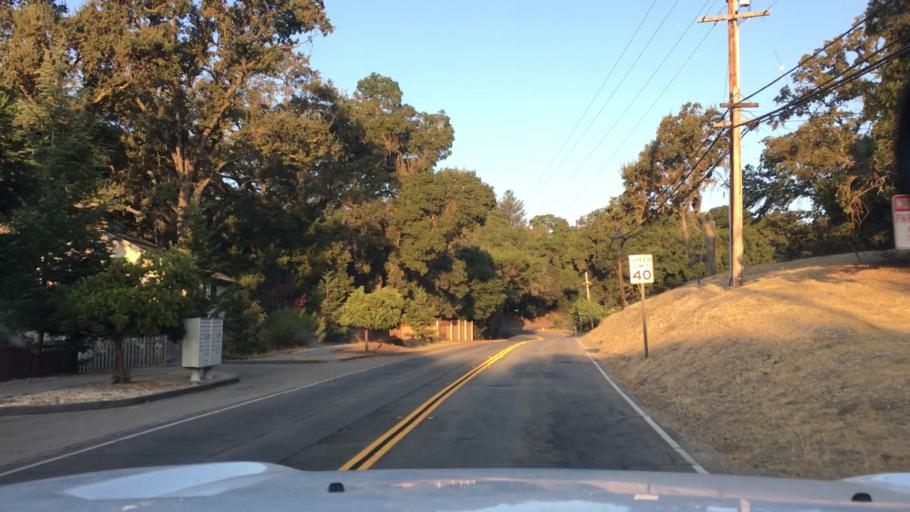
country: US
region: California
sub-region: San Luis Obispo County
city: Atascadero
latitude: 35.4840
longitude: -120.6767
